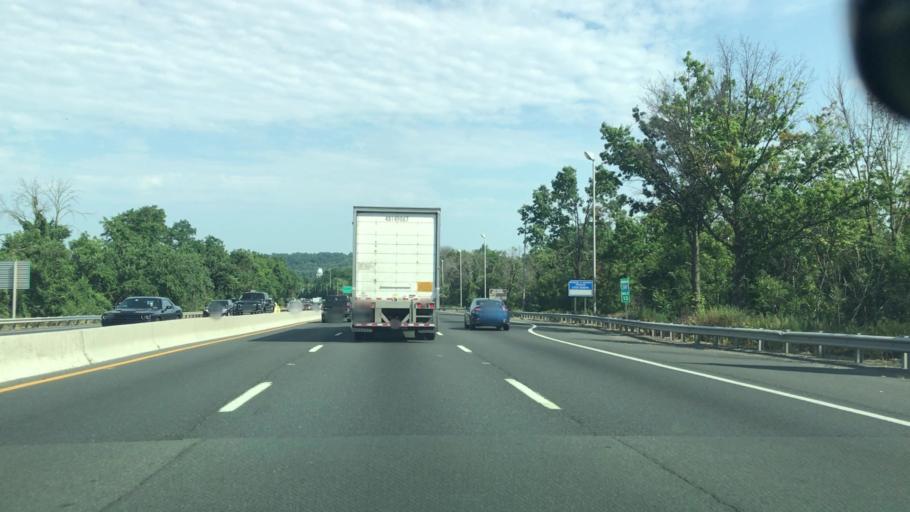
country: US
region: New Jersey
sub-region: Somerset County
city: Bound Brook
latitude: 40.5618
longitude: -74.5501
